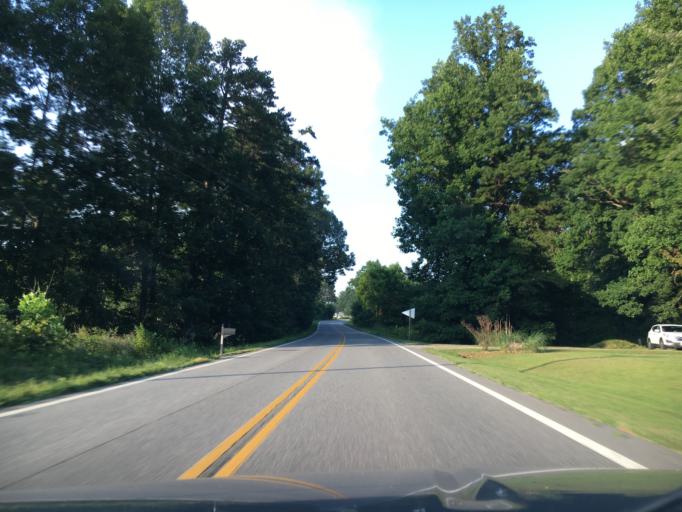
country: US
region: Virginia
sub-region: Halifax County
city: Mountain Road
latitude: 36.8336
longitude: -79.0668
